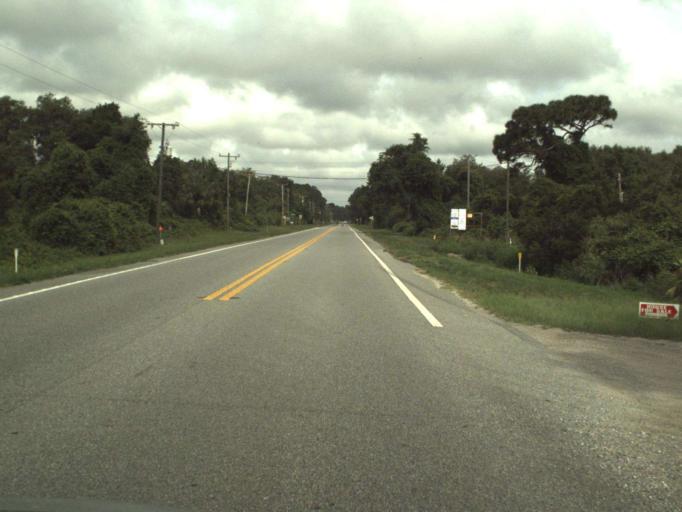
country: US
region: Florida
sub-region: Seminole County
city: Geneva
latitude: 28.7242
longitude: -81.0933
